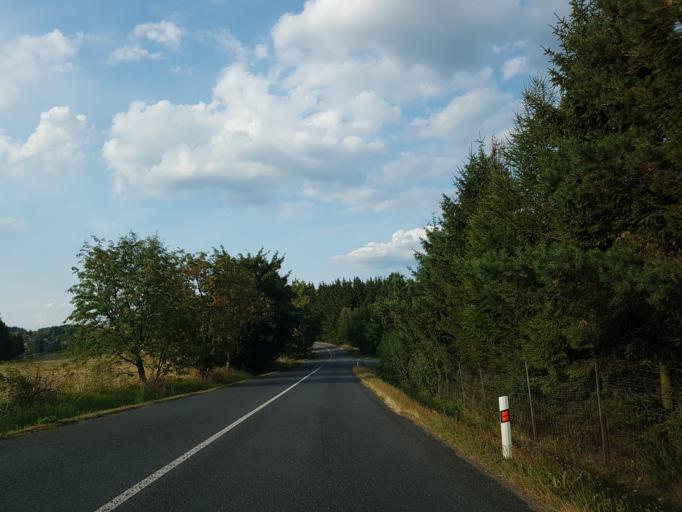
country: CZ
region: Liberecky
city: Mala Skala
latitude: 50.6725
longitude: 15.1824
